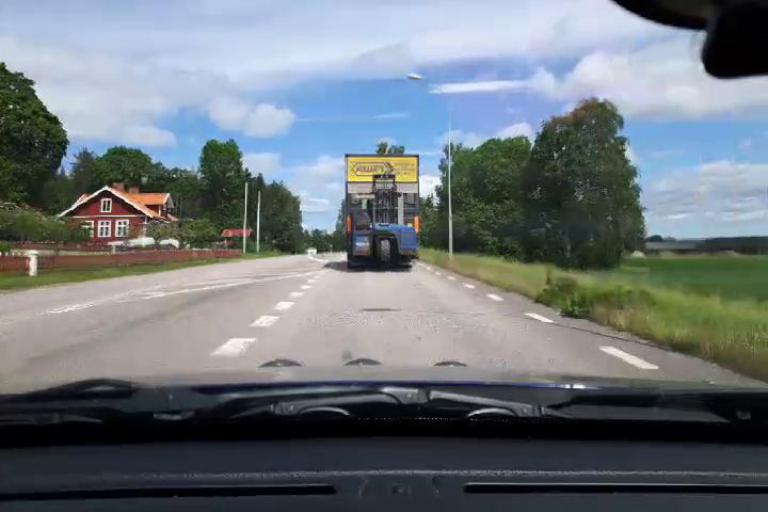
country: SE
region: Uppsala
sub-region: Osthammars Kommun
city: Bjorklinge
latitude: 60.0858
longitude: 17.5502
